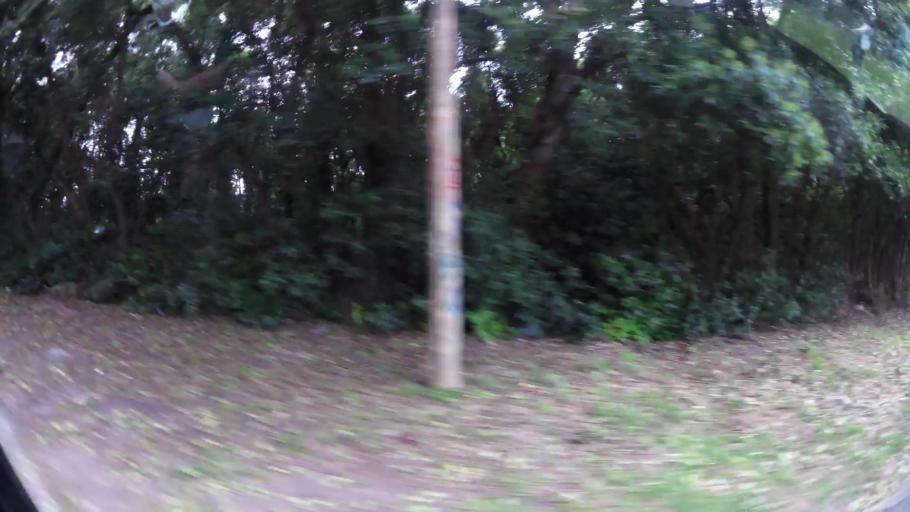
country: AR
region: Buenos Aires
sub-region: Partido de La Plata
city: La Plata
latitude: -34.9351
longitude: -57.9874
